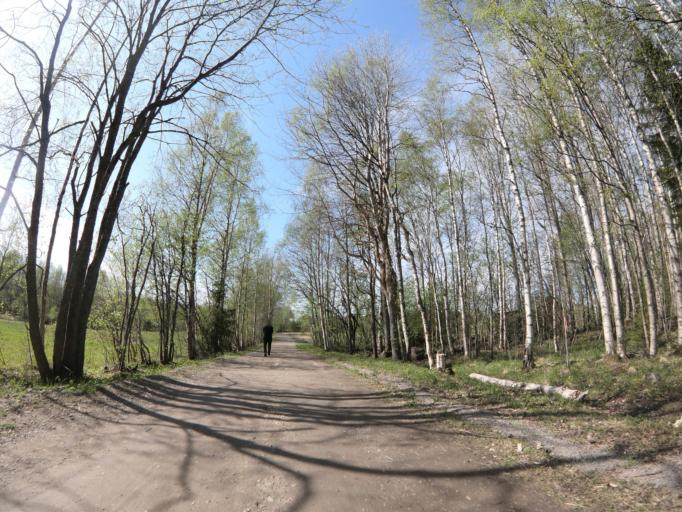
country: SE
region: Vaesterbotten
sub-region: Umea Kommun
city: Roback
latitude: 63.8281
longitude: 20.2015
